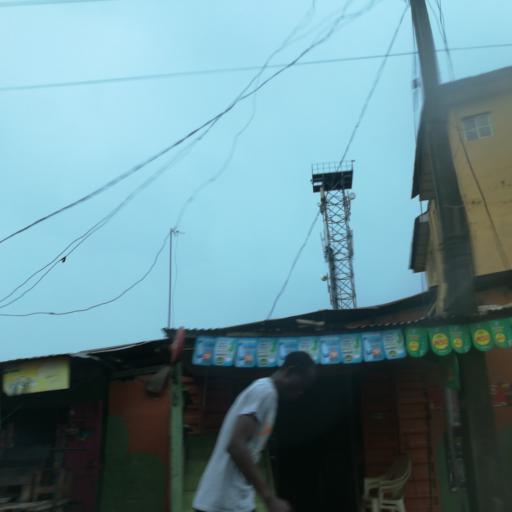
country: NG
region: Lagos
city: Oshodi
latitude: 6.5564
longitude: 3.3427
